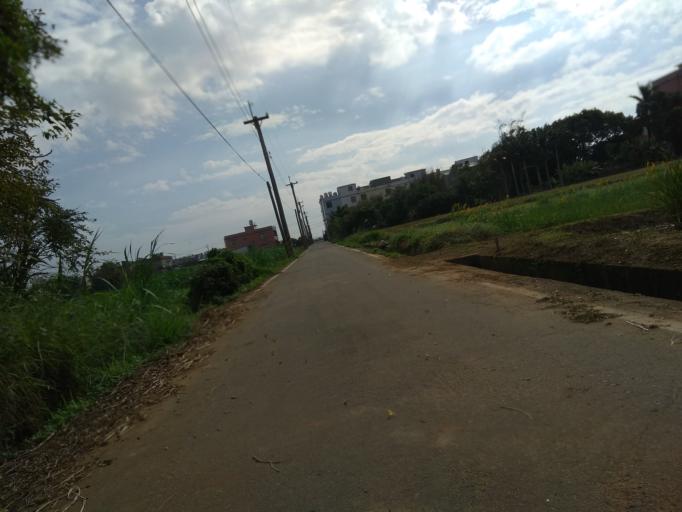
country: TW
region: Taiwan
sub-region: Hsinchu
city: Zhubei
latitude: 24.9491
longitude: 121.0032
